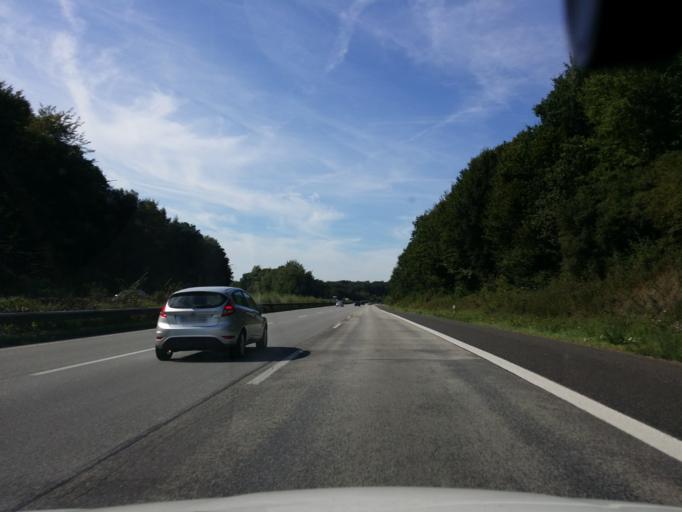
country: DE
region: Rheinland-Pfalz
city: Ebernhahn
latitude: 50.4577
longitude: 7.7734
